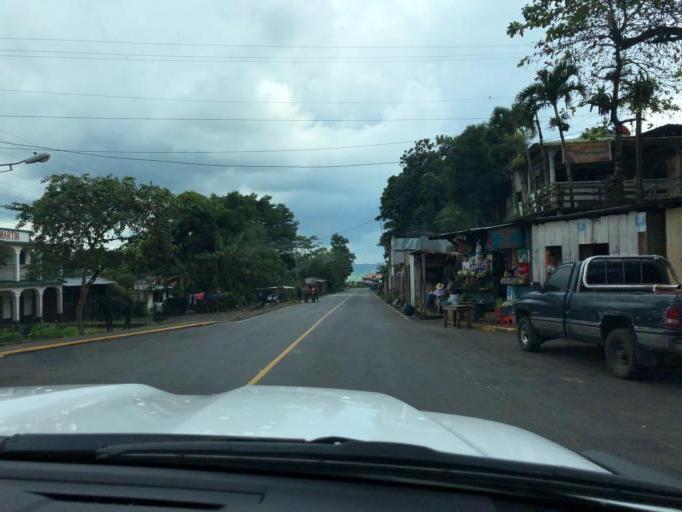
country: NI
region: Chontales
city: Villa Sandino
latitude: 11.9992
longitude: -84.7786
